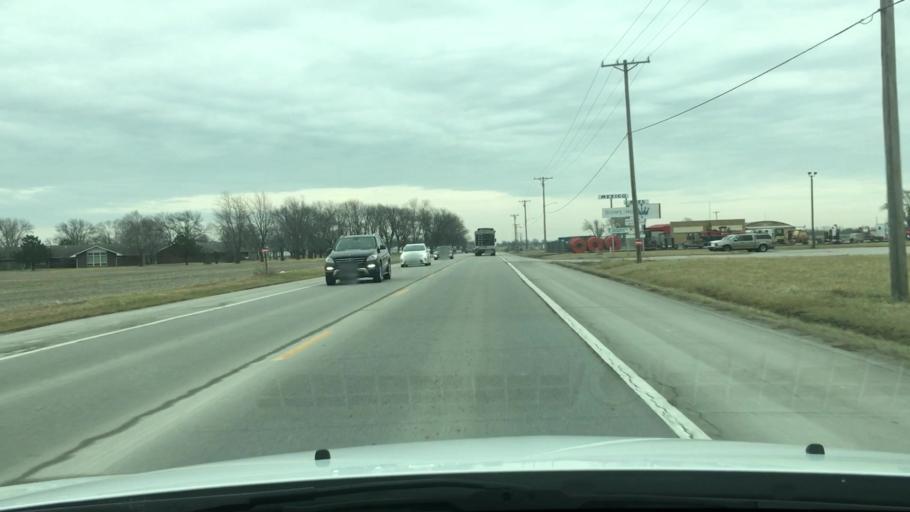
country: US
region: Missouri
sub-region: Audrain County
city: Mexico
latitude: 39.1635
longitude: -91.8279
